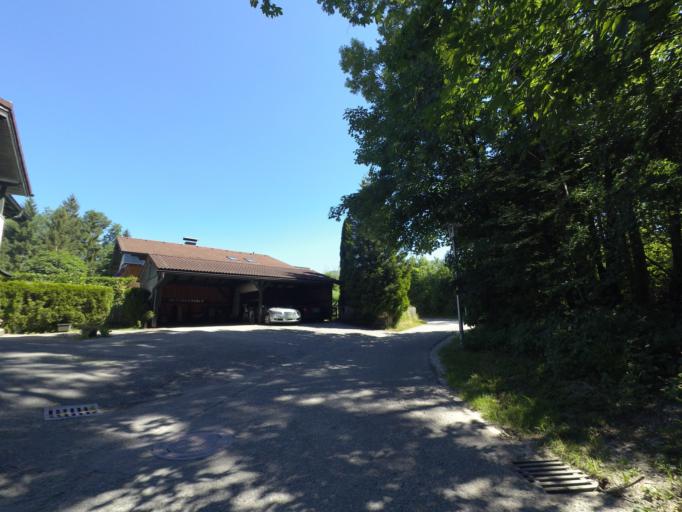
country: AT
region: Salzburg
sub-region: Politischer Bezirk Hallein
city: Puch bei Hallein
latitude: 47.7296
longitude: 13.0816
